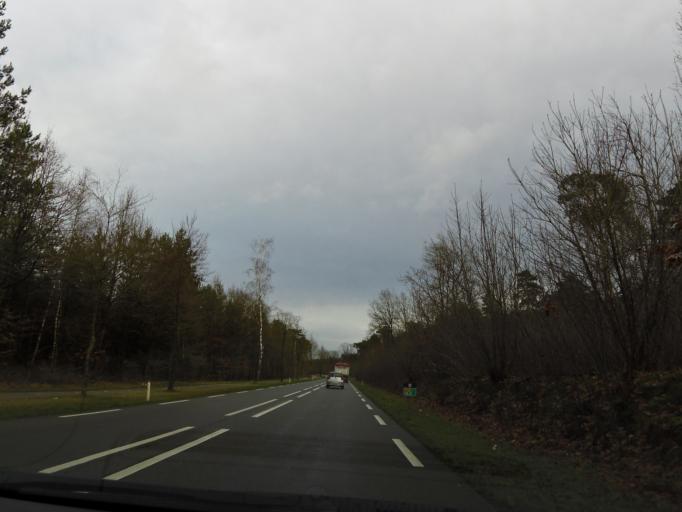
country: NL
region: Limburg
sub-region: Gemeente Roerdalen
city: Posterholt
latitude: 51.1030
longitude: 6.0119
